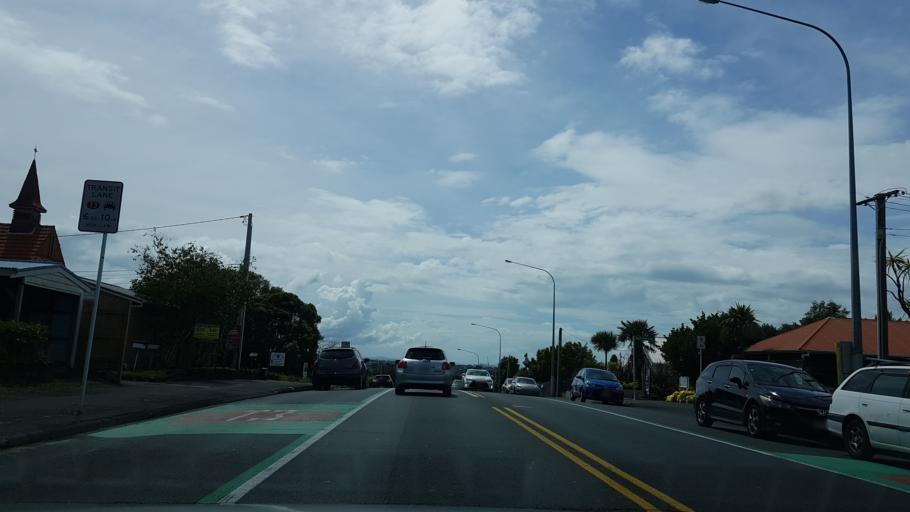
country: NZ
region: Auckland
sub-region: Auckland
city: North Shore
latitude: -36.8105
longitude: 174.7391
